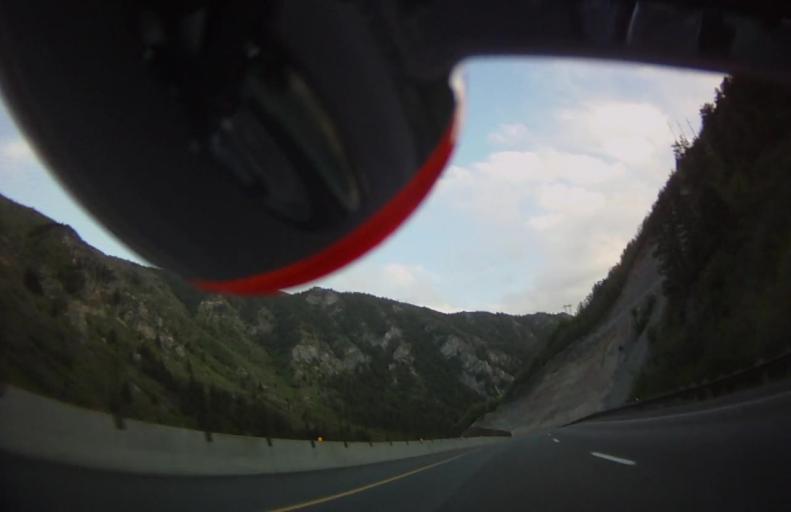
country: US
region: Utah
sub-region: Utah County
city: Orem
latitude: 40.3729
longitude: -111.5555
